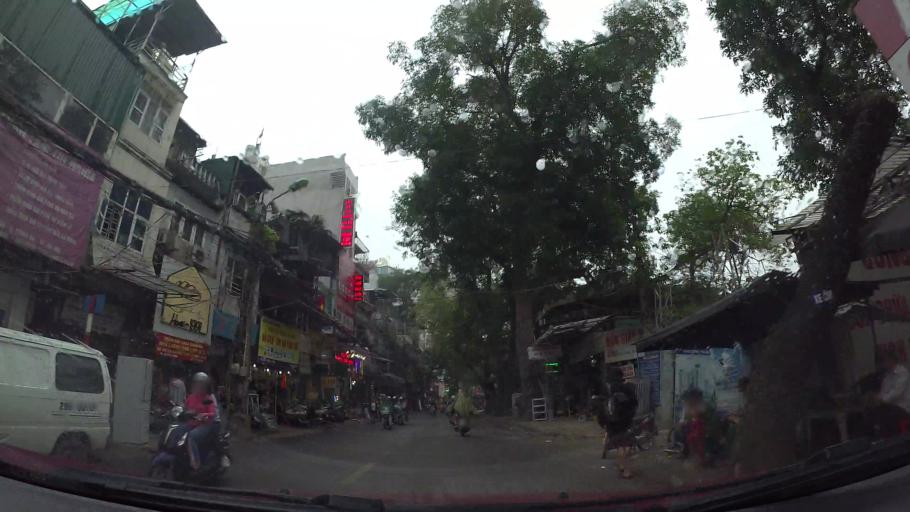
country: VN
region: Ha Noi
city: Dong Da
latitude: 21.0233
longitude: 105.8205
